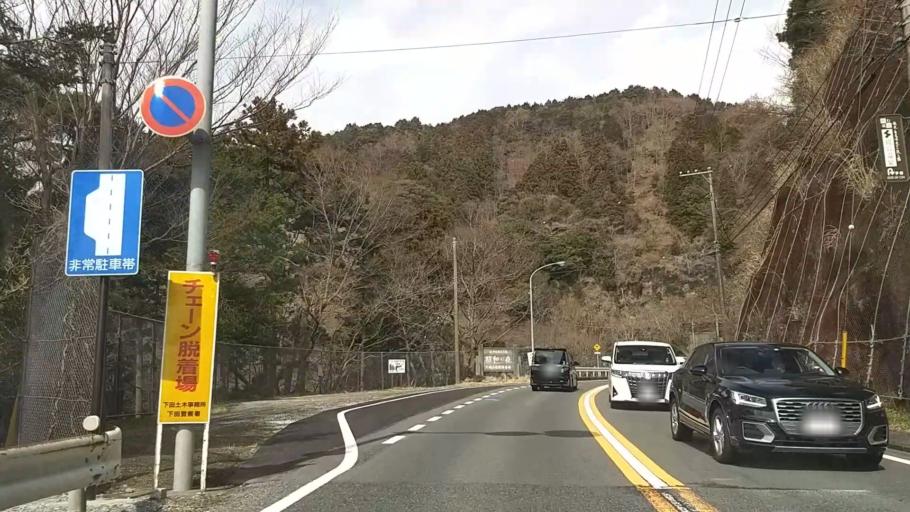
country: JP
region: Shizuoka
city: Shimoda
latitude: 34.8084
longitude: 138.9294
